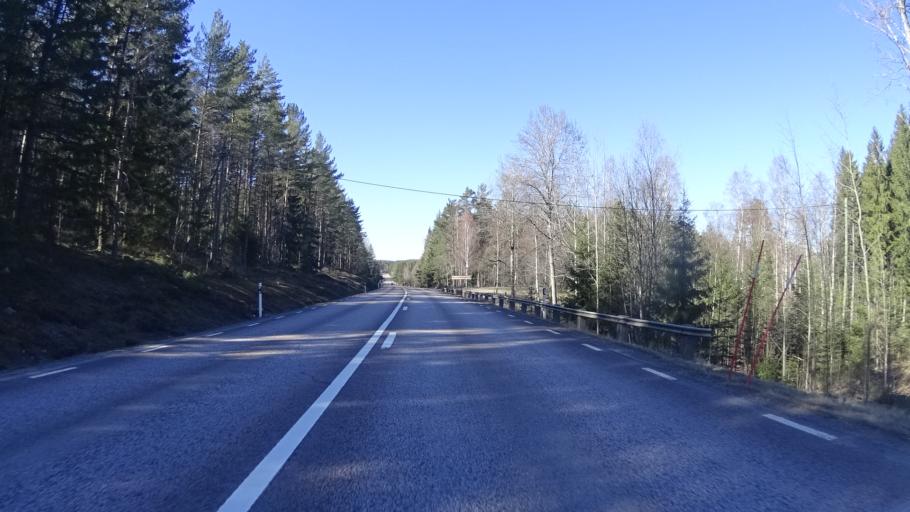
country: SE
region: Vaermland
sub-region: Karlstads Kommun
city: Edsvalla
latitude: 59.5955
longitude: 13.0068
